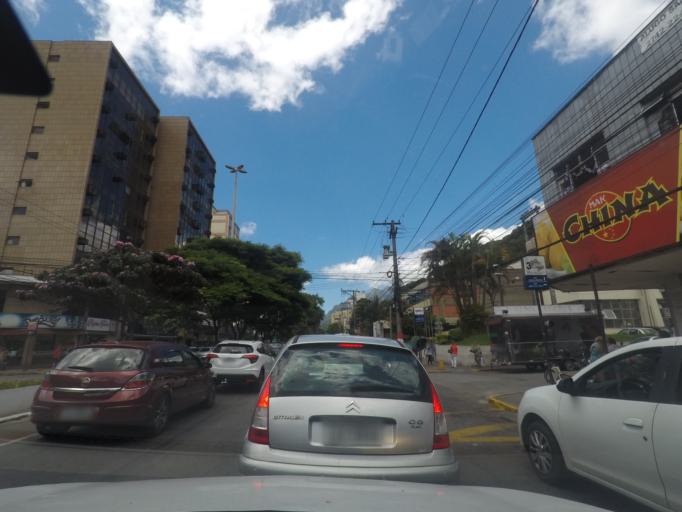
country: BR
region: Rio de Janeiro
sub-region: Teresopolis
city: Teresopolis
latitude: -22.4112
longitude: -42.9685
